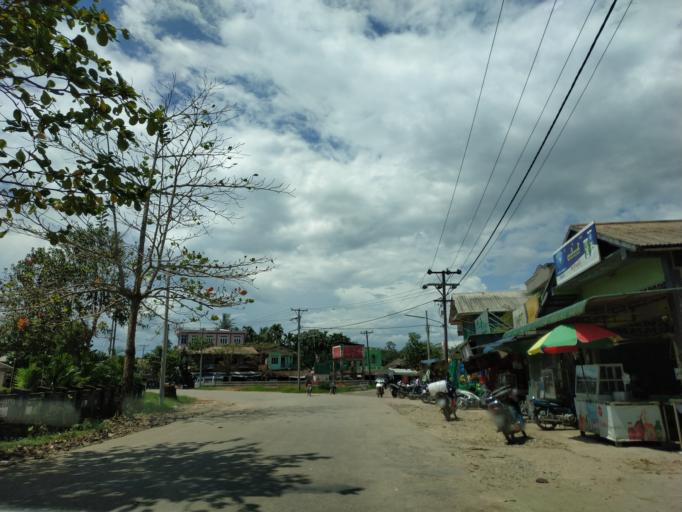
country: MM
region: Tanintharyi
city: Dawei
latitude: 14.1040
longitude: 98.1719
